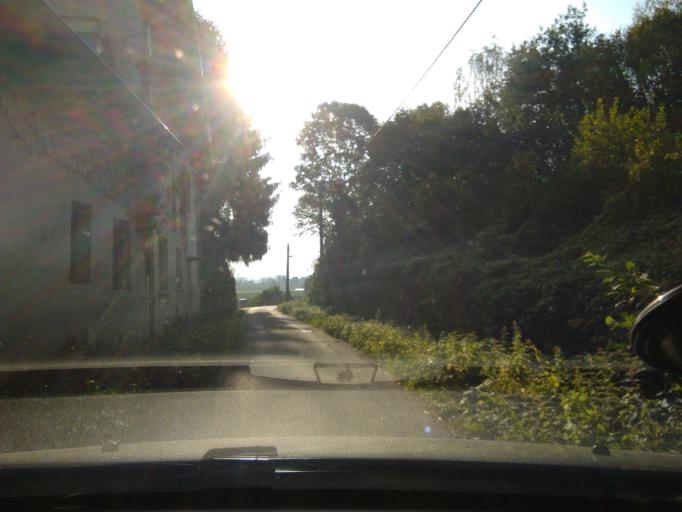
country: DE
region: Saxony
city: Niederau
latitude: 51.1442
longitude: 13.5181
